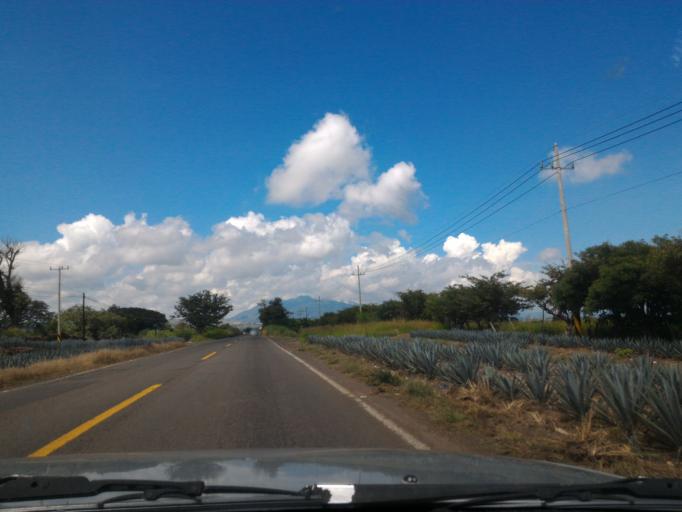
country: MX
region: Jalisco
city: Tequila
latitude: 20.8725
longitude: -103.7997
